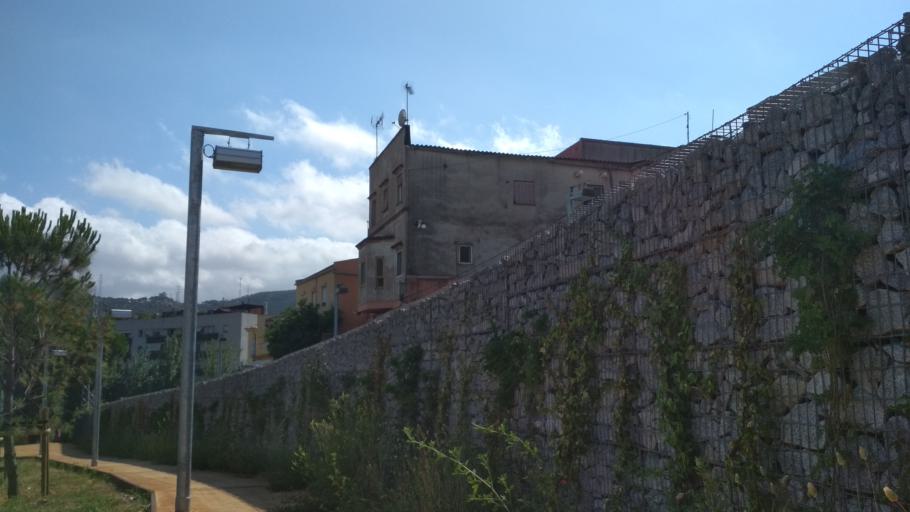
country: ES
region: Catalonia
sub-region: Provincia de Barcelona
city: Montcada i Reixac
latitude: 41.4669
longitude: 2.1863
